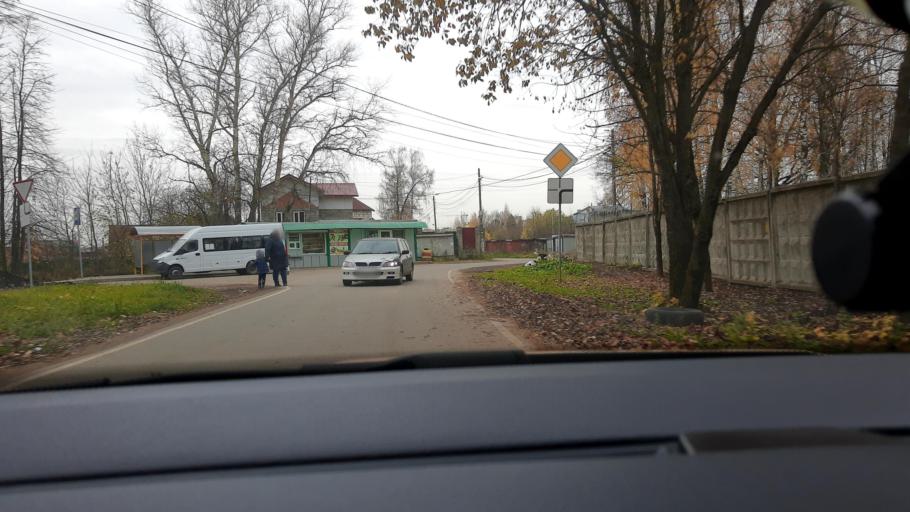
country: RU
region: Moskovskaya
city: Pirogovskiy
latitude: 55.9597
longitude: 37.7300
